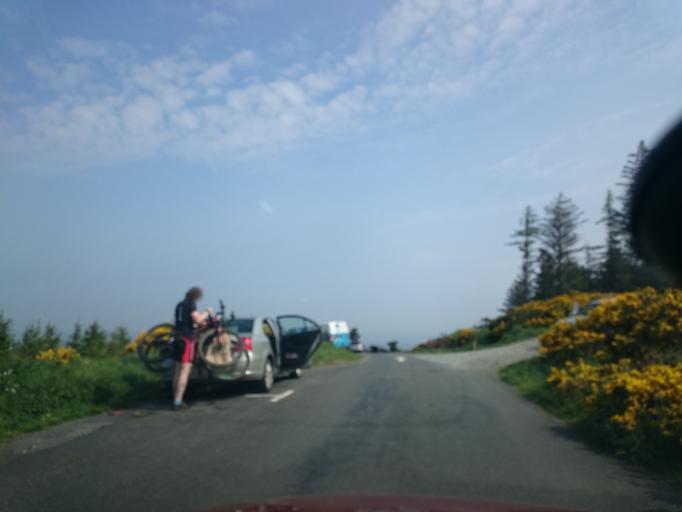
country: IE
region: Leinster
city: Ballinteer
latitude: 53.2528
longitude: -6.2474
